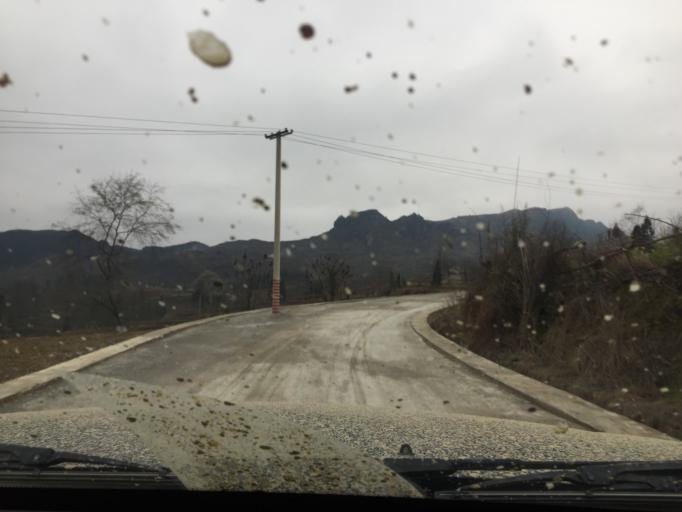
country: CN
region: Guizhou Sheng
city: Changfeng
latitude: 28.4927
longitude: 108.0543
